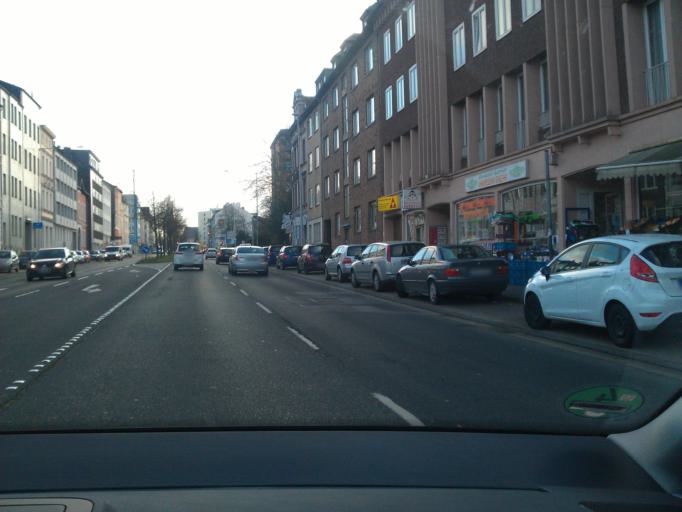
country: DE
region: North Rhine-Westphalia
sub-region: Regierungsbezirk Koln
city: Aachen
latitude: 50.7857
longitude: 6.0720
